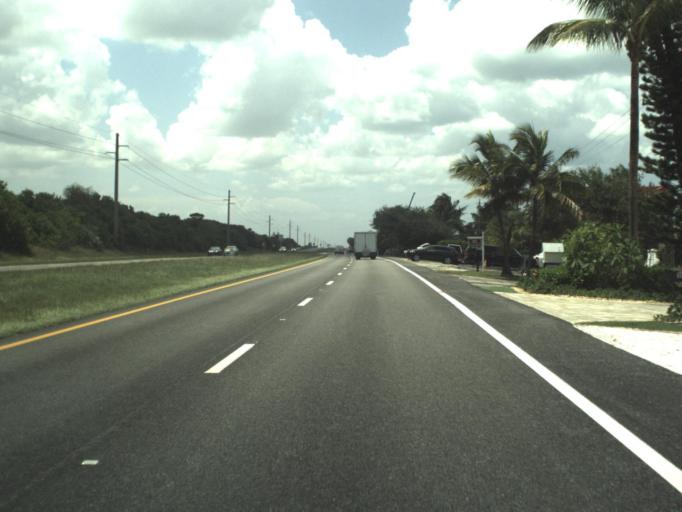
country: US
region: Florida
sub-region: Palm Beach County
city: Tequesta
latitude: 26.9848
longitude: -80.0920
